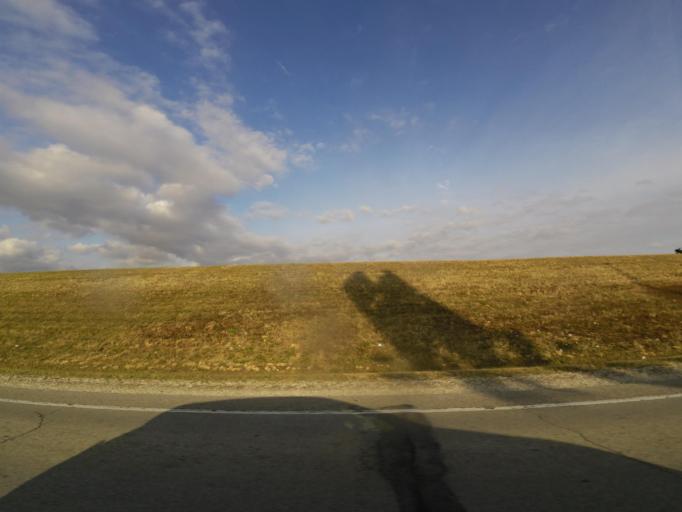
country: US
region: Illinois
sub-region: Fayette County
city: Vandalia
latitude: 38.9752
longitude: -89.1185
